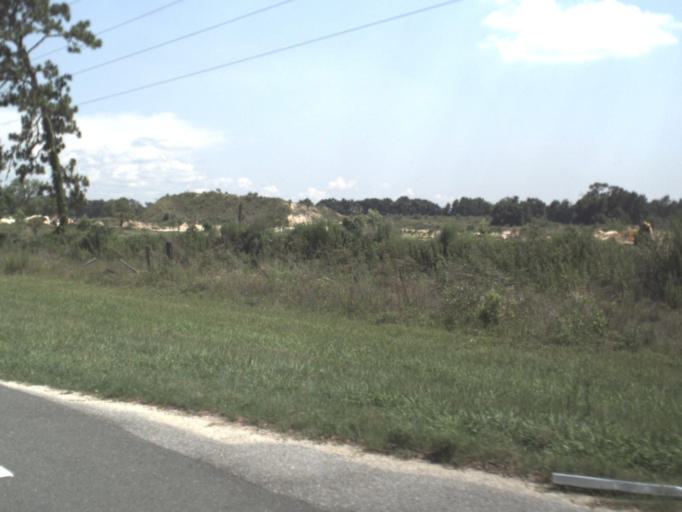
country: US
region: Florida
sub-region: Lafayette County
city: Mayo
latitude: 30.0915
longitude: -83.2299
